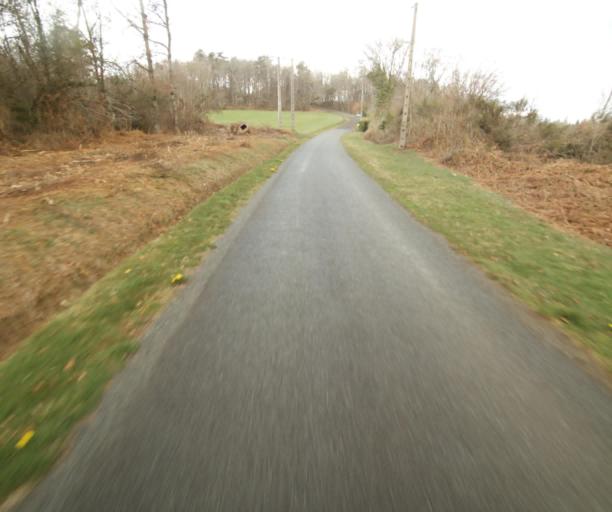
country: FR
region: Limousin
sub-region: Departement de la Correze
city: Saint-Privat
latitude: 45.2537
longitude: 1.9982
